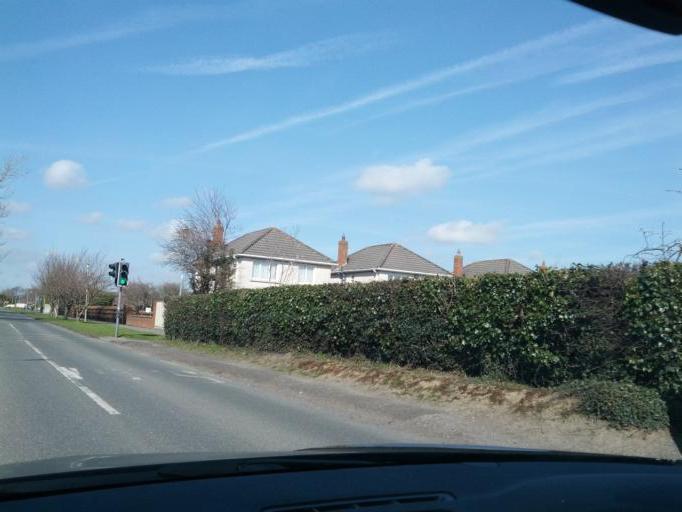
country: IE
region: Leinster
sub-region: Kildare
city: Maynooth
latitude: 53.3718
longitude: -6.5837
